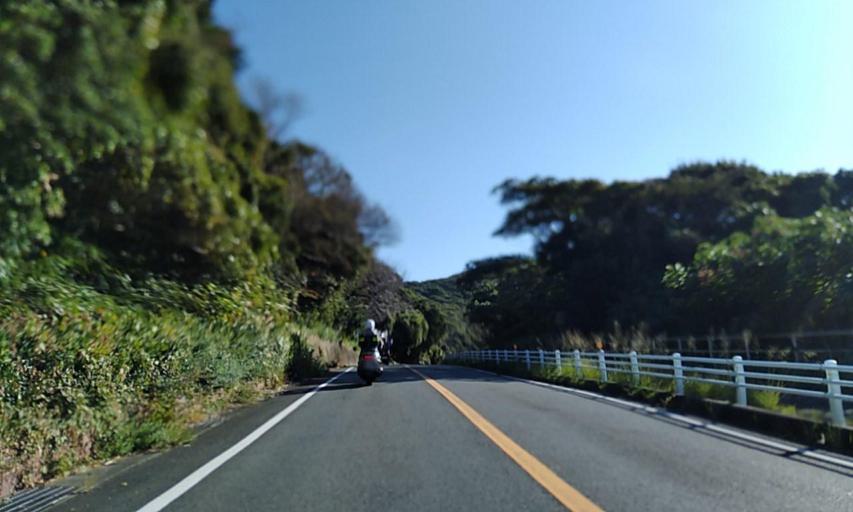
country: JP
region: Aichi
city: Toyohama
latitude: 34.5820
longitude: 137.0317
